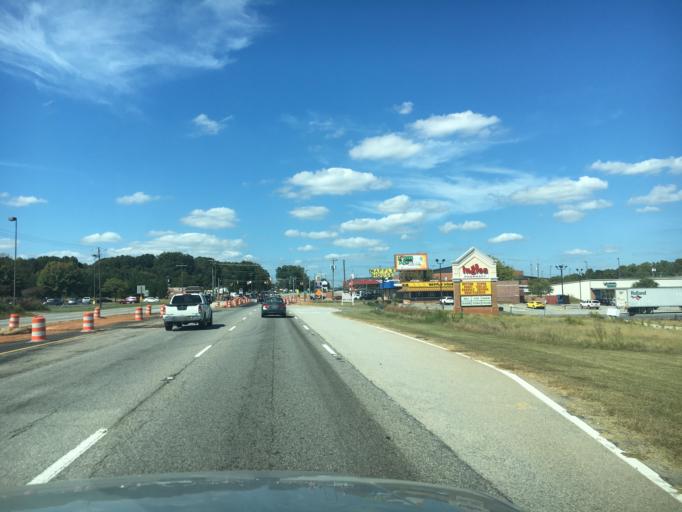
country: US
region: South Carolina
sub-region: Spartanburg County
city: Southern Shops
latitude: 35.0008
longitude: -82.0052
